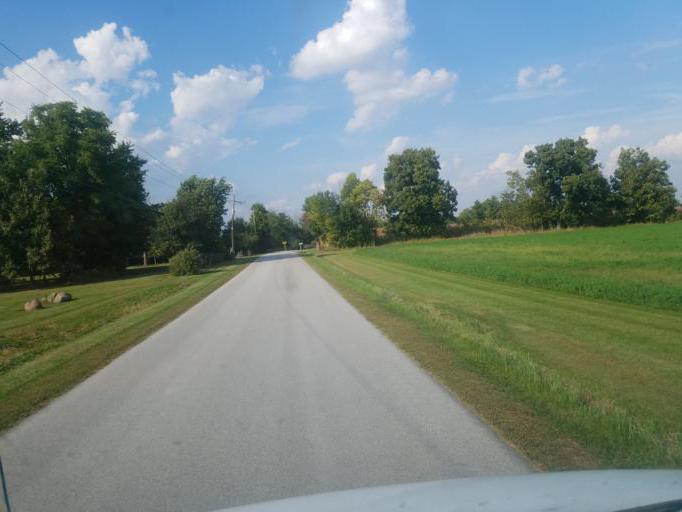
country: US
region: Ohio
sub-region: Hancock County
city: Arlington
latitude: 40.8790
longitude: -83.5709
